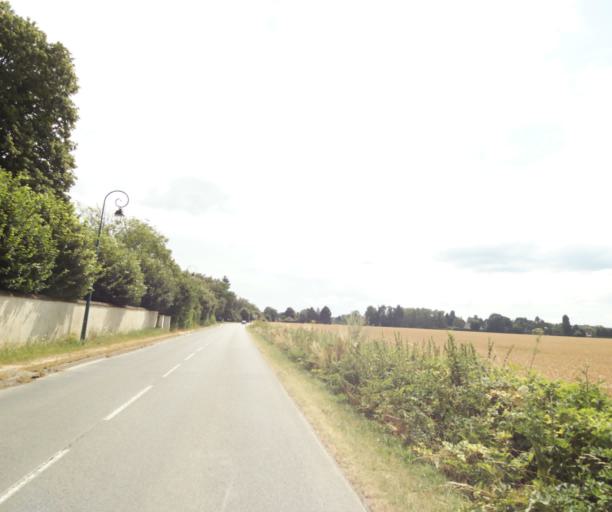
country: FR
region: Ile-de-France
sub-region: Departement de Seine-et-Marne
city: Barbizon
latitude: 48.4522
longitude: 2.6042
